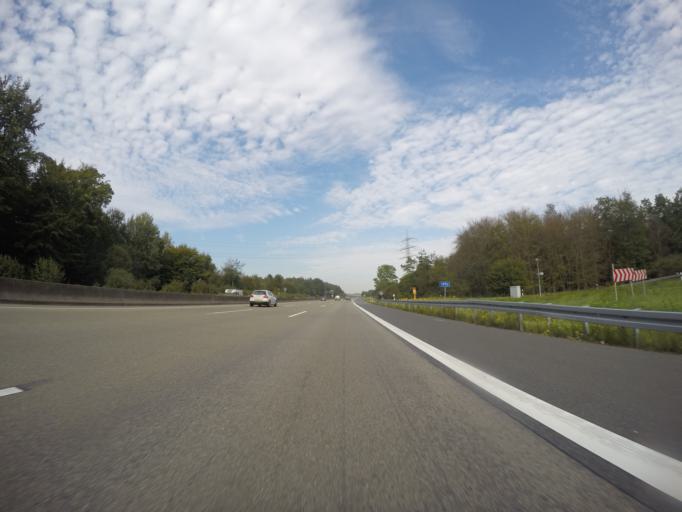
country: DE
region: Hesse
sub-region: Regierungsbezirk Darmstadt
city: Seligenstadt
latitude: 50.0333
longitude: 8.9380
